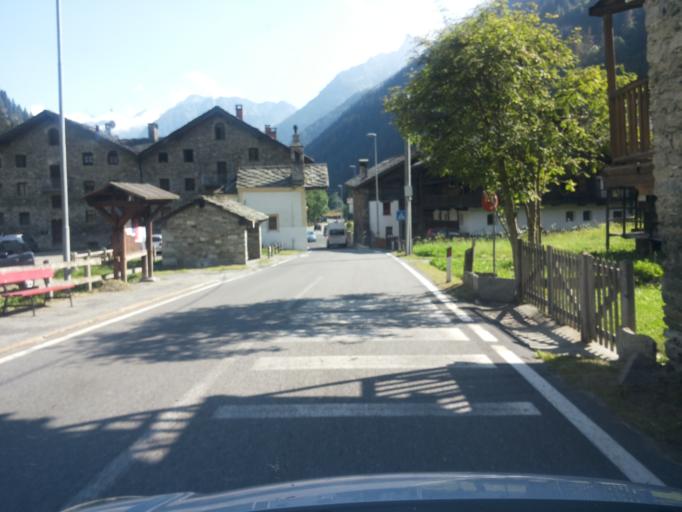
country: IT
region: Aosta Valley
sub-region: Valle d'Aosta
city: Gressoney-La-Trinite
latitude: 45.8013
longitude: 7.8236
